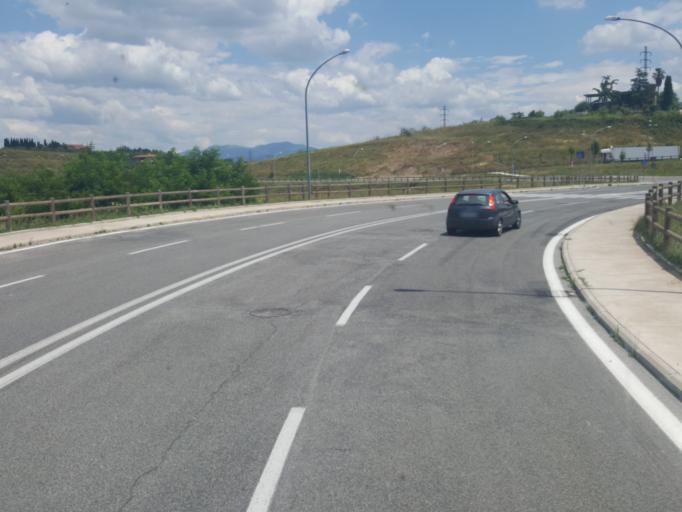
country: IT
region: Latium
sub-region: Citta metropolitana di Roma Capitale
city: Fiano Romano
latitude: 42.1658
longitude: 12.6488
